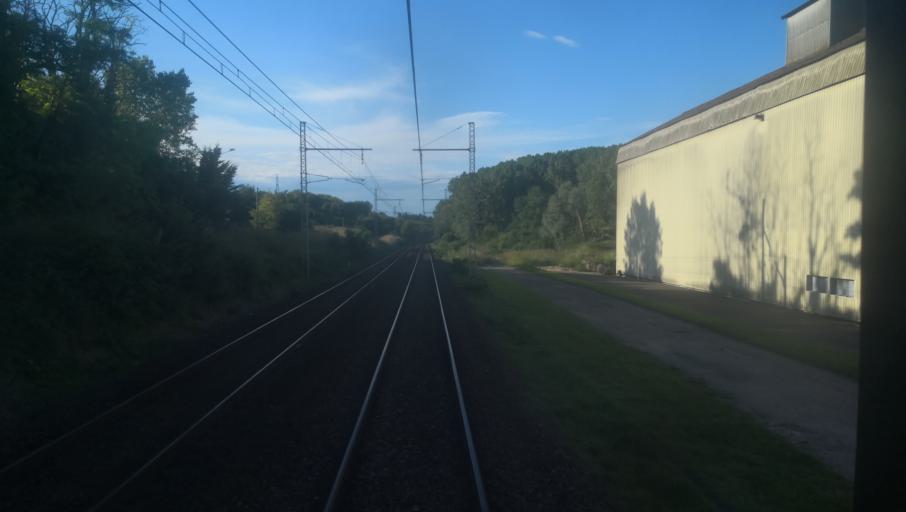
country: FR
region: Centre
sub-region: Departement de l'Indre
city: Reuilly
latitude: 47.0958
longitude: 2.0461
